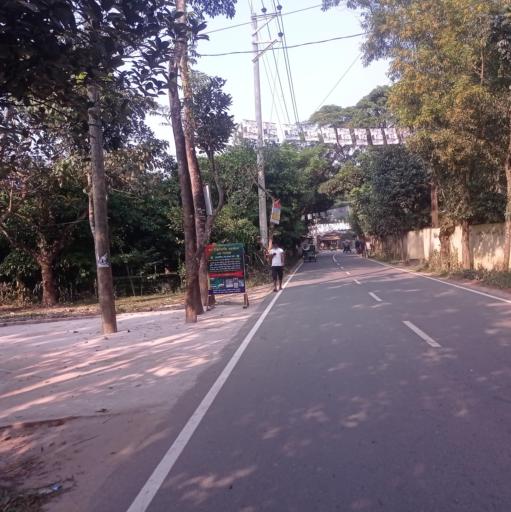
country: BD
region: Dhaka
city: Bhairab Bazar
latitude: 24.0383
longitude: 90.8321
